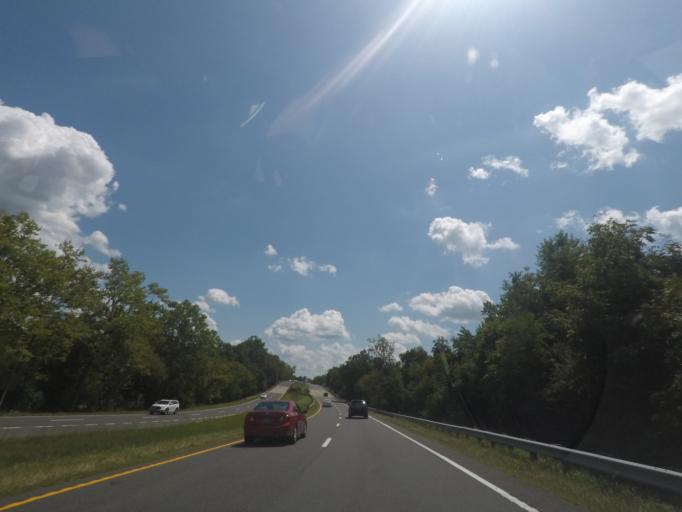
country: US
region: Virginia
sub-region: City of Winchester
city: Winchester
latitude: 39.0984
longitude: -78.1107
